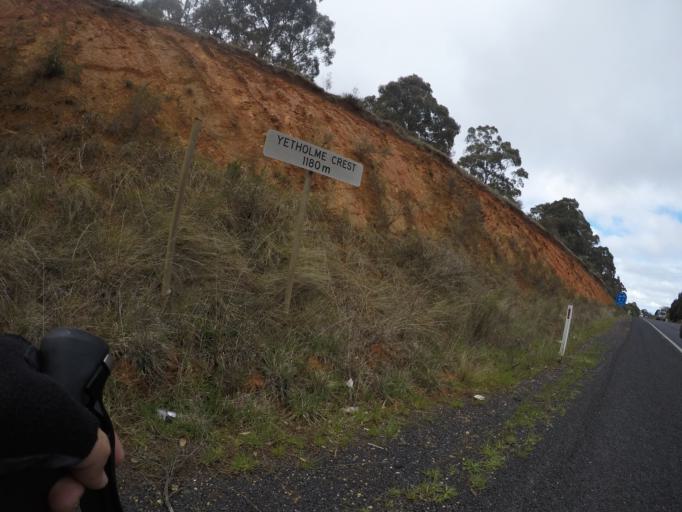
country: AU
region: New South Wales
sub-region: Lithgow
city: Portland
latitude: -33.4423
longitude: 149.8359
